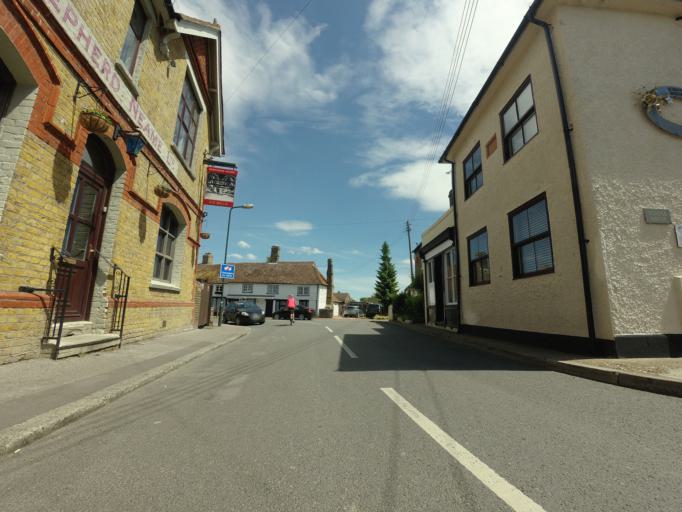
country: GB
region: England
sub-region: Kent
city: Cliffe
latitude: 51.4612
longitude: 0.4979
